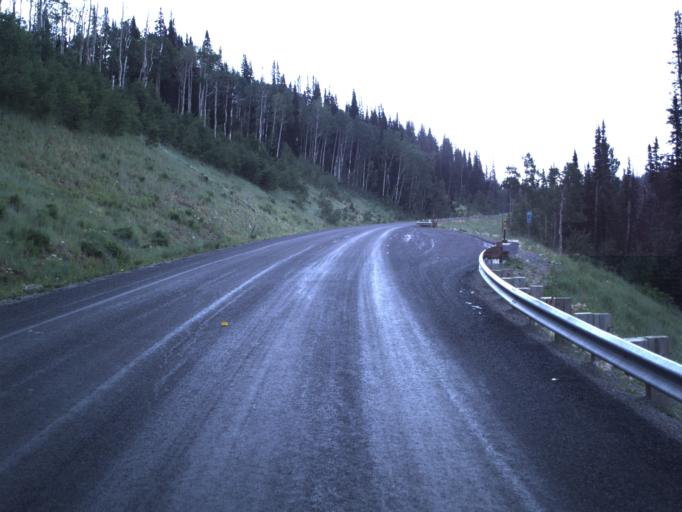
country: US
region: Utah
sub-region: Summit County
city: Francis
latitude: 40.5004
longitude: -111.0413
